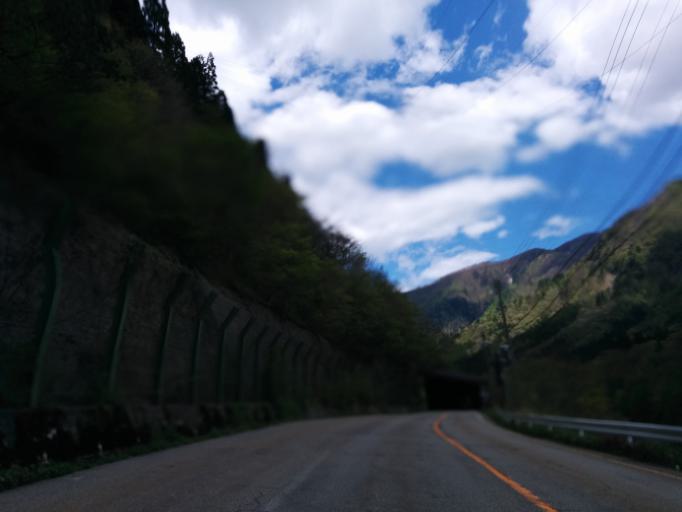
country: JP
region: Toyama
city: Fukumitsu
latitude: 36.3252
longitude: 136.8894
